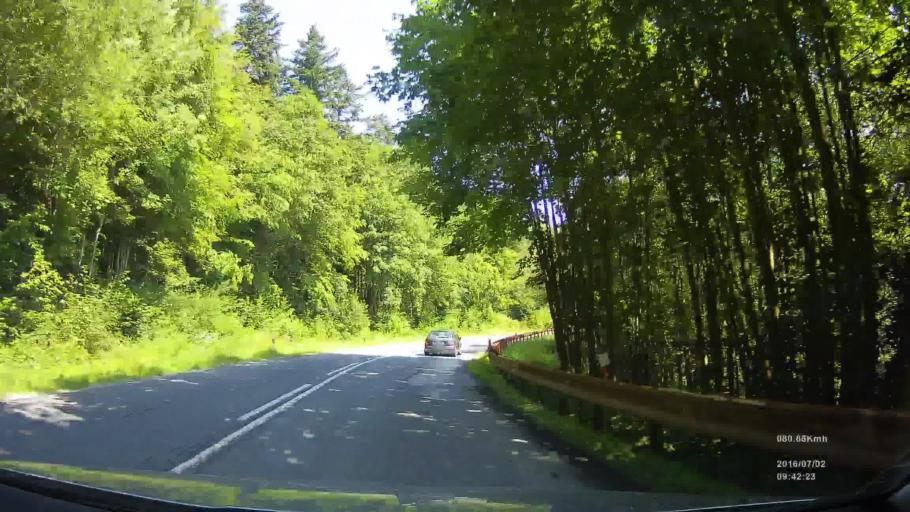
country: SK
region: Kosicky
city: Gelnica
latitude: 48.8412
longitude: 21.0360
